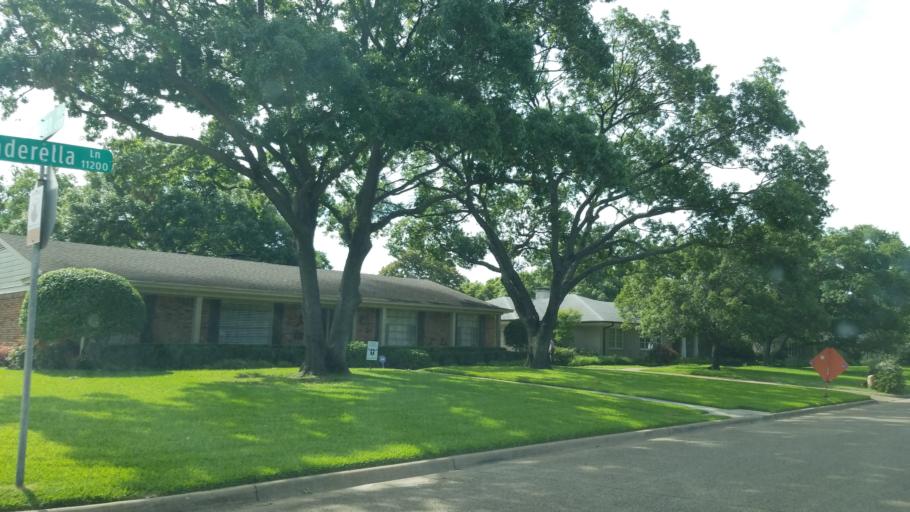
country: US
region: Texas
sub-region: Dallas County
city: Addison
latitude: 32.9021
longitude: -96.8396
